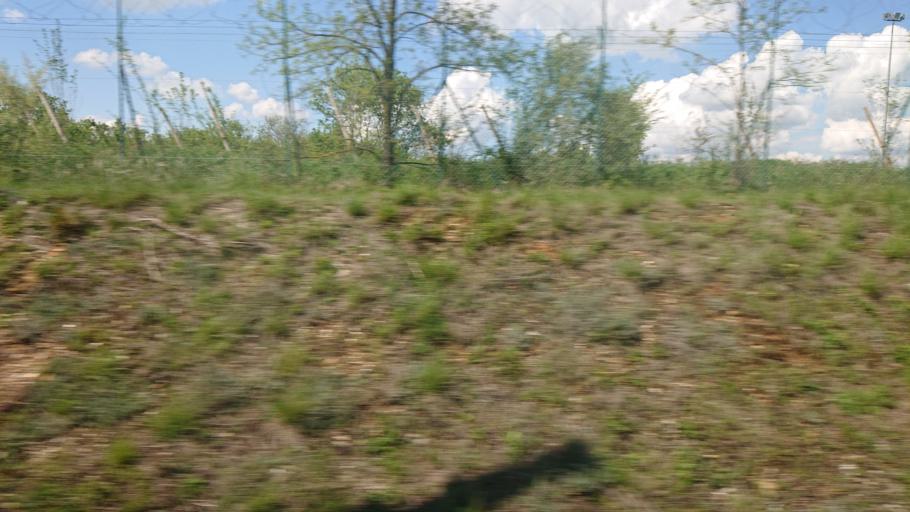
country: FR
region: Rhone-Alpes
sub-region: Departement de l'Ain
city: Leyment
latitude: 45.9283
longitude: 5.2631
